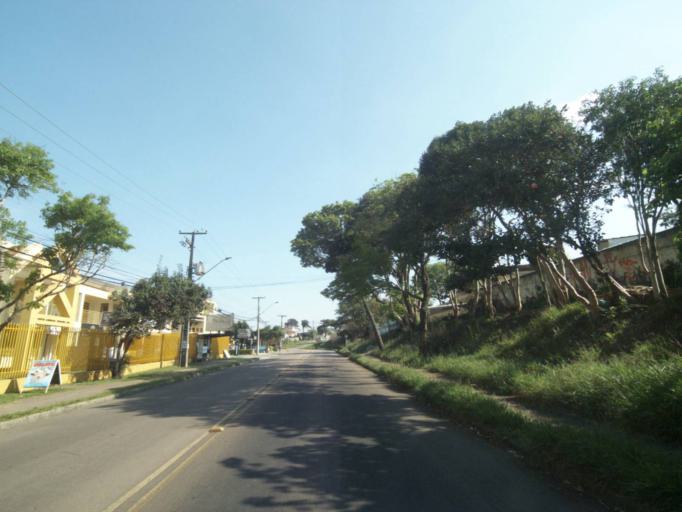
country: BR
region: Parana
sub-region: Curitiba
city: Curitiba
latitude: -25.4812
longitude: -49.3229
